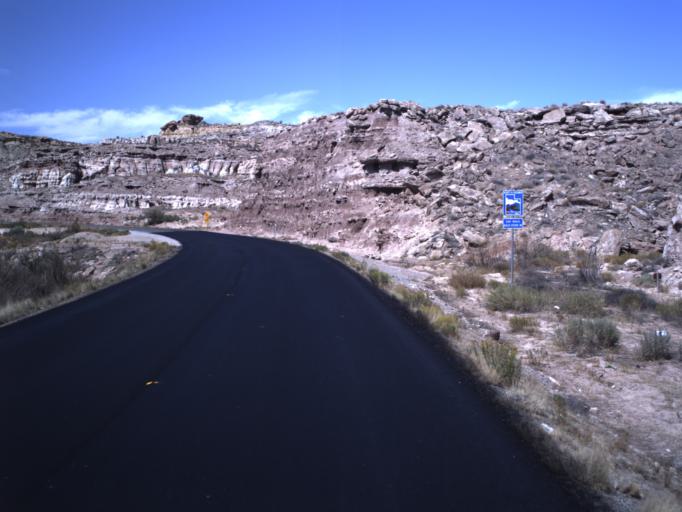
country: US
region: Utah
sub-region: San Juan County
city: Blanding
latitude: 37.2576
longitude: -109.2647
